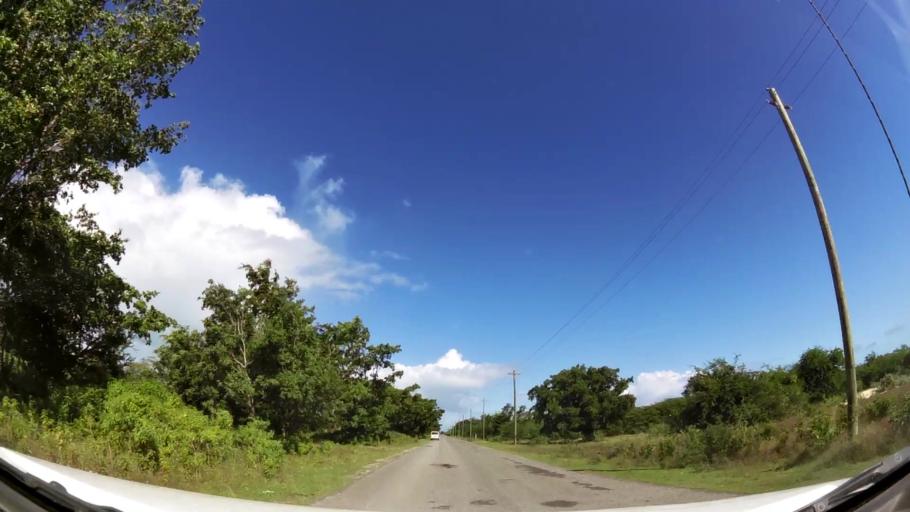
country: AG
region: Barbuda
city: Codrington
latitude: 17.6067
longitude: -61.8288
